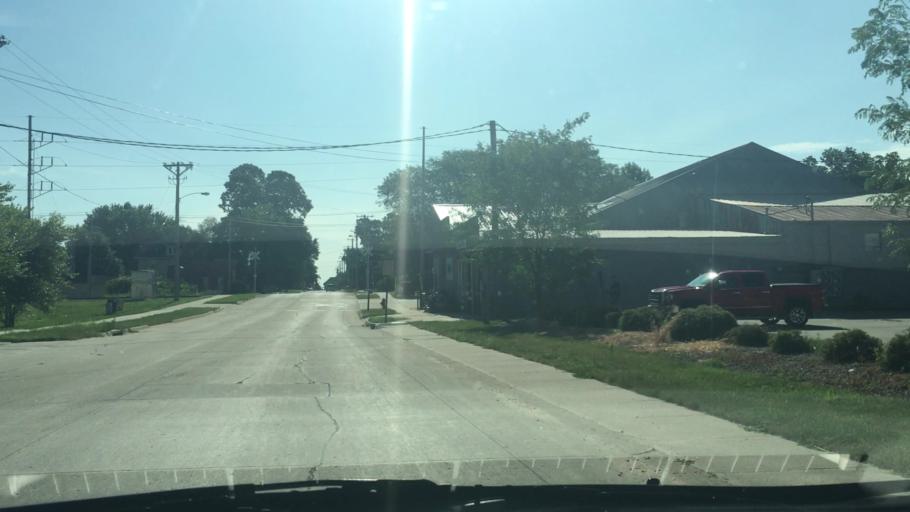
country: US
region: Iowa
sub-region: Johnson County
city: North Liberty
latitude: 41.7485
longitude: -91.6039
